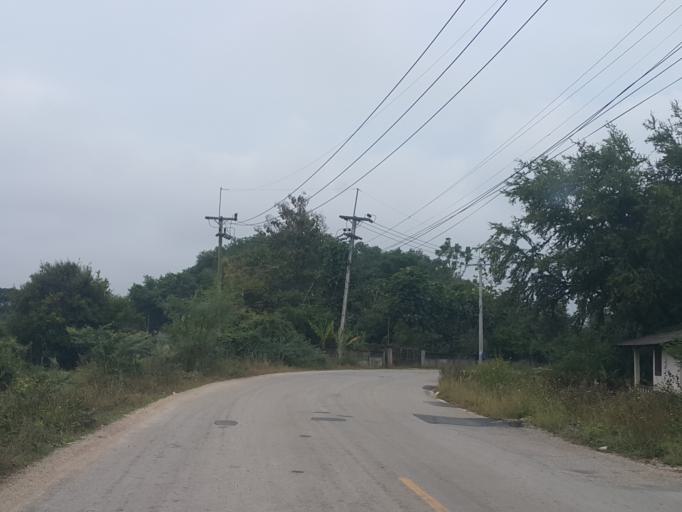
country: TH
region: Lampang
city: Lampang
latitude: 18.3249
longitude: 99.4886
